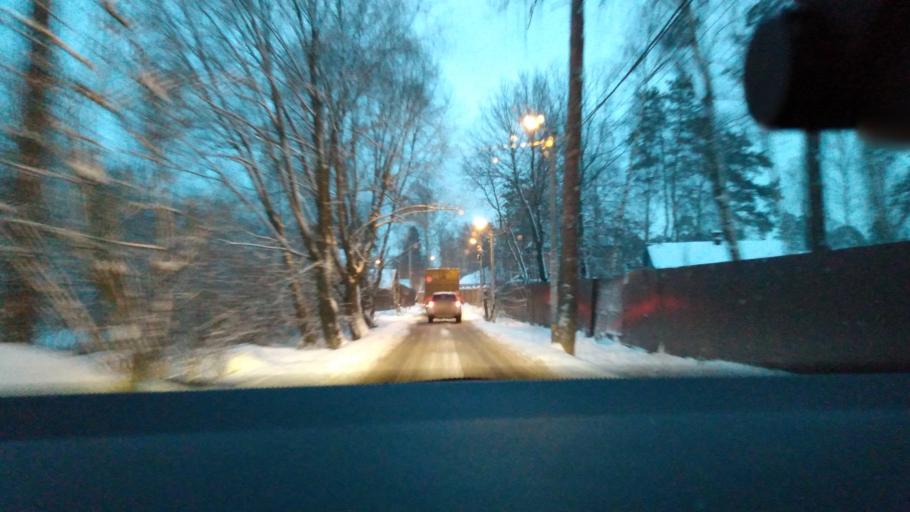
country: RU
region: Moskovskaya
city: Saltykovka
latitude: 55.7647
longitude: 37.9294
